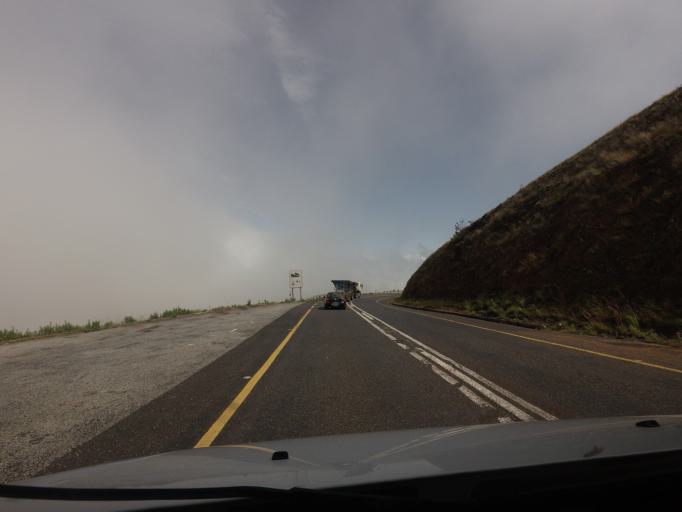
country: ZA
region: Mpumalanga
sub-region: Ehlanzeni District
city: Lydenburg
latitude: -25.1611
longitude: 30.6283
